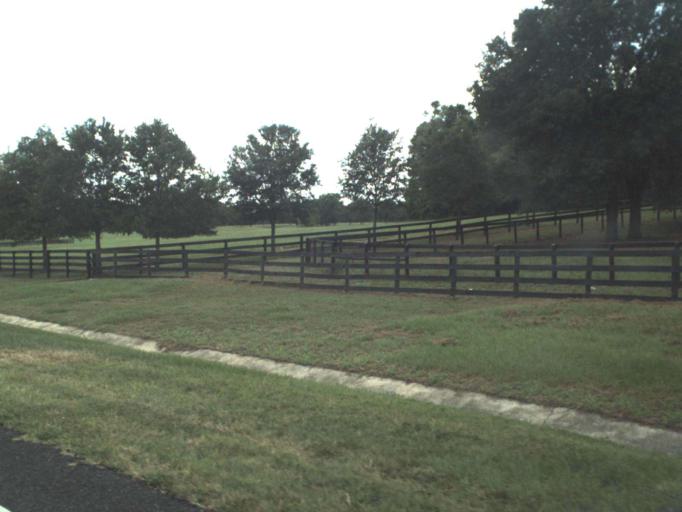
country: US
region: Florida
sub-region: Marion County
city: Citra
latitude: 29.3165
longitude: -82.1519
